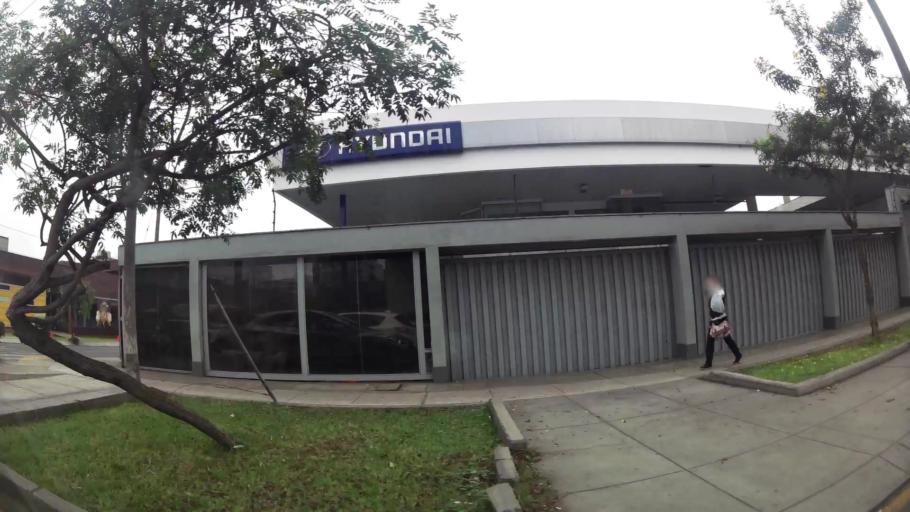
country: PE
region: Lima
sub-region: Lima
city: San Isidro
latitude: -12.1140
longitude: -77.0348
